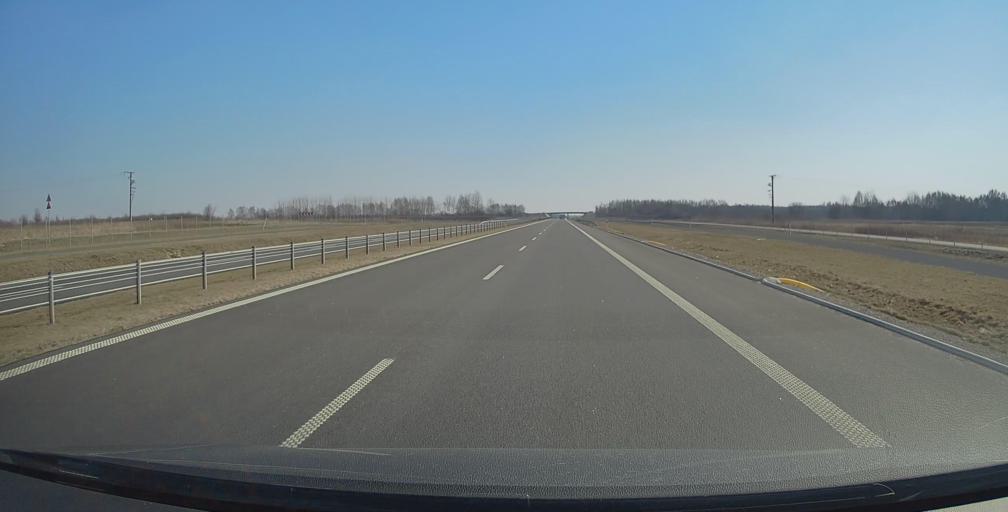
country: PL
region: Lublin Voivodeship
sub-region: Powiat janowski
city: Modliborzyce
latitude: 50.7396
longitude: 22.3247
